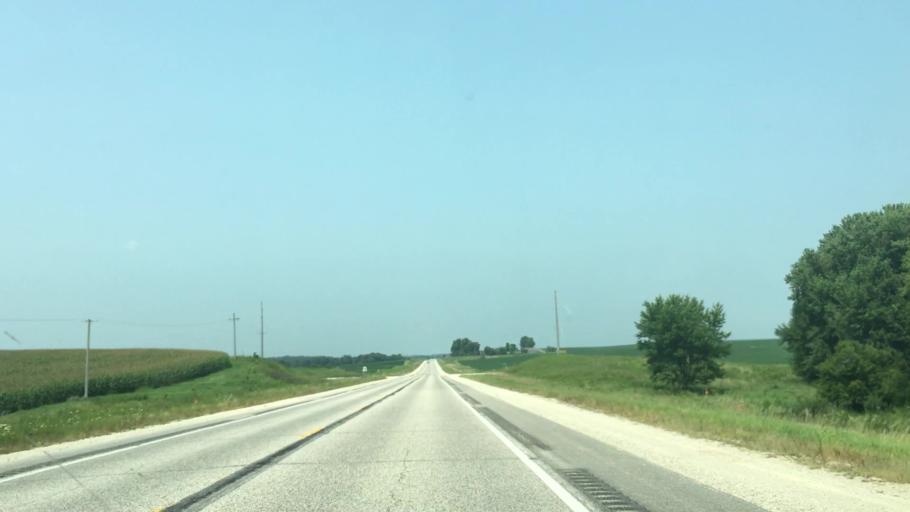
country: US
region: Iowa
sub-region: Fayette County
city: Fayette
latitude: 42.7868
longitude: -91.8048
